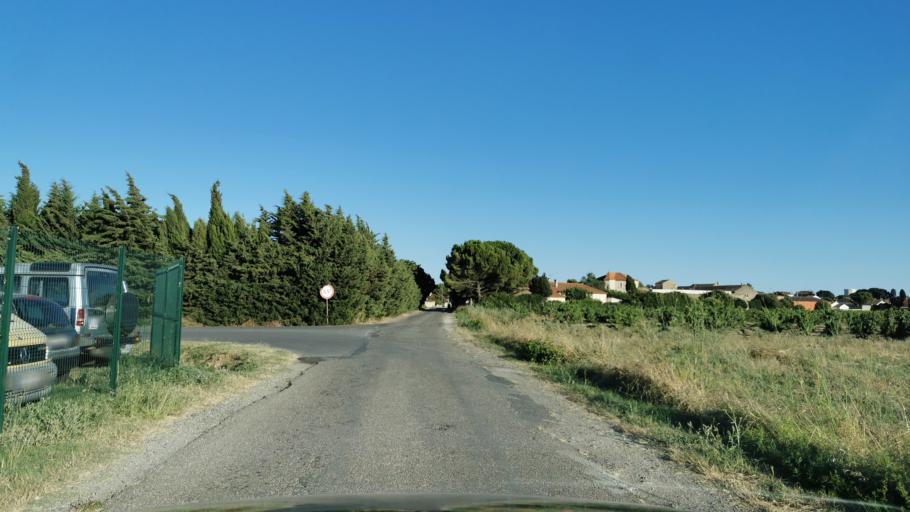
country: FR
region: Languedoc-Roussillon
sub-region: Departement de l'Aude
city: Ouveillan
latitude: 43.2518
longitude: 2.9952
